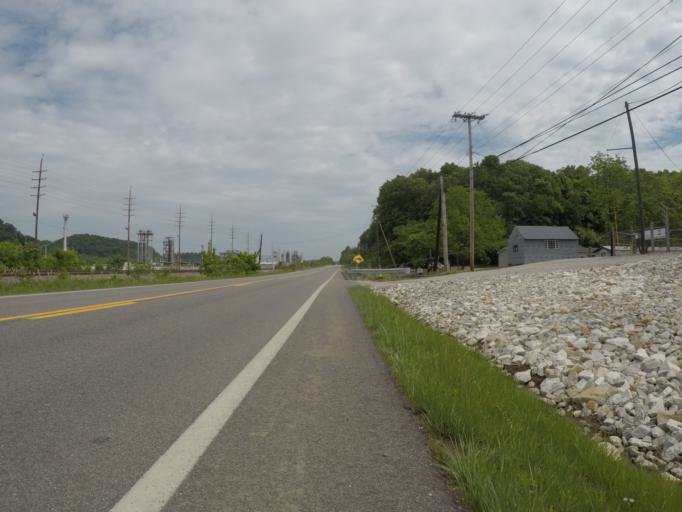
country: US
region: West Virginia
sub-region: Wayne County
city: Kenova
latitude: 38.3492
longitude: -82.5934
